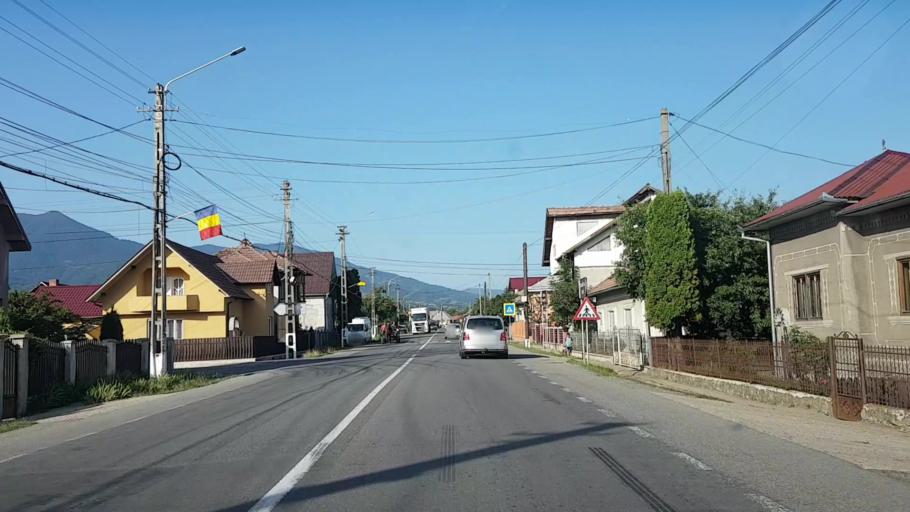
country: RO
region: Bistrita-Nasaud
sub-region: Comuna Josenii Bargaului
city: Josenii Bargaului
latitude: 47.2117
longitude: 24.6708
